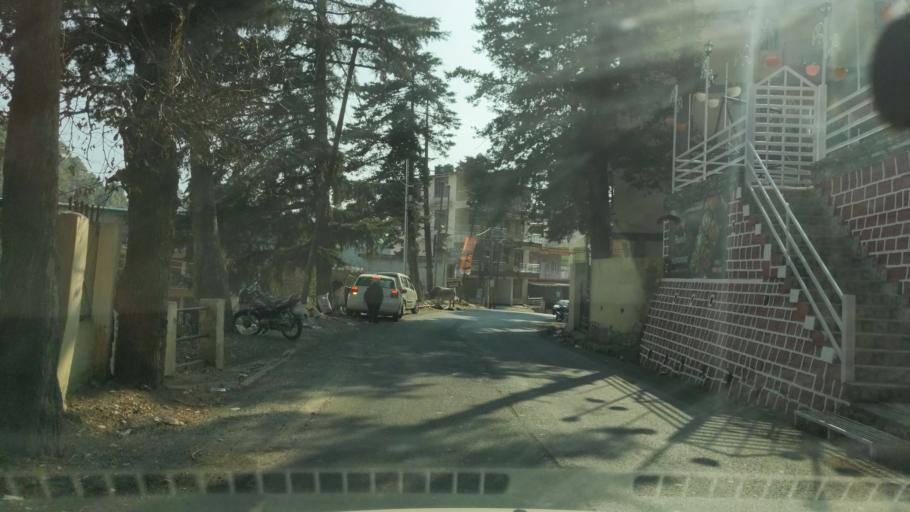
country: IN
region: Uttarakhand
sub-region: Naini Tal
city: Bhowali
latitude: 29.3866
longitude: 79.5289
